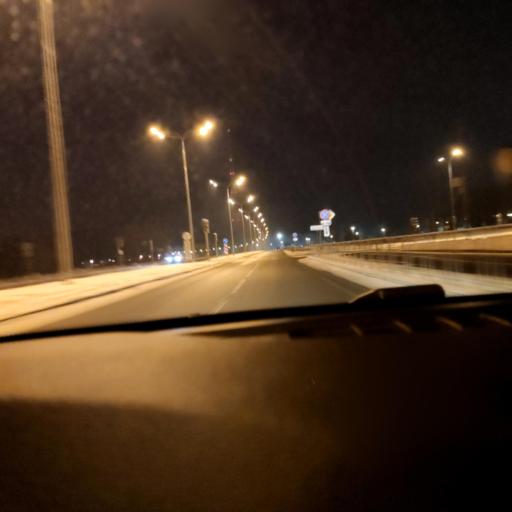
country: RU
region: Samara
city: Samara
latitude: 53.2866
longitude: 50.2341
